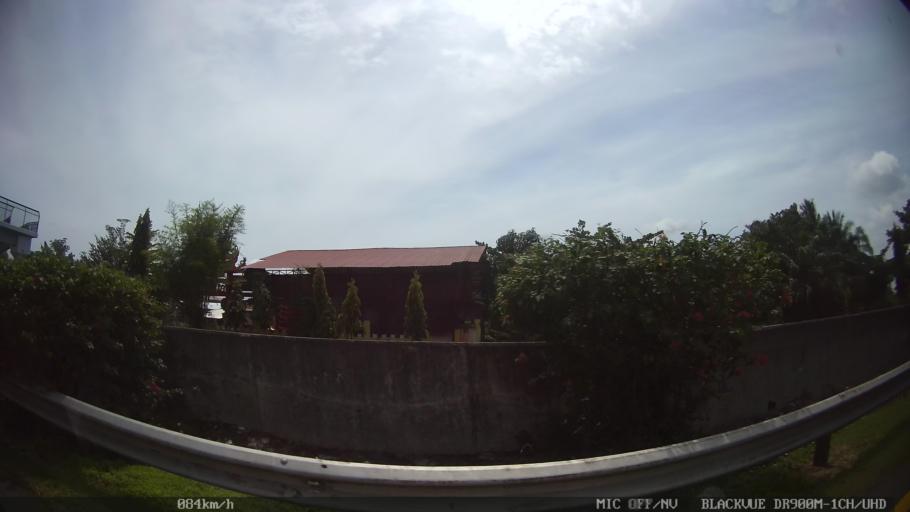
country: ID
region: North Sumatra
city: Labuhan Deli
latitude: 3.7169
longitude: 98.6826
